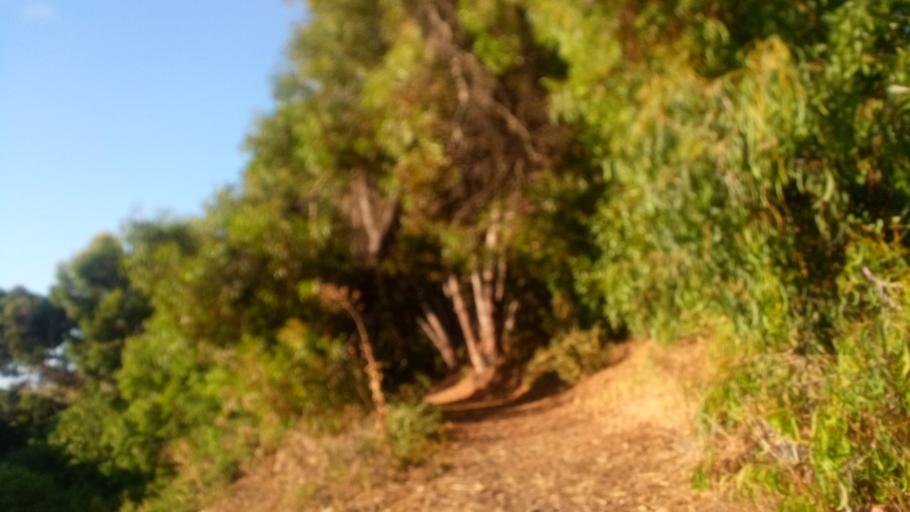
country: PT
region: Faro
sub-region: Tavira
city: Tavira
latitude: 37.1436
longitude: -7.5822
